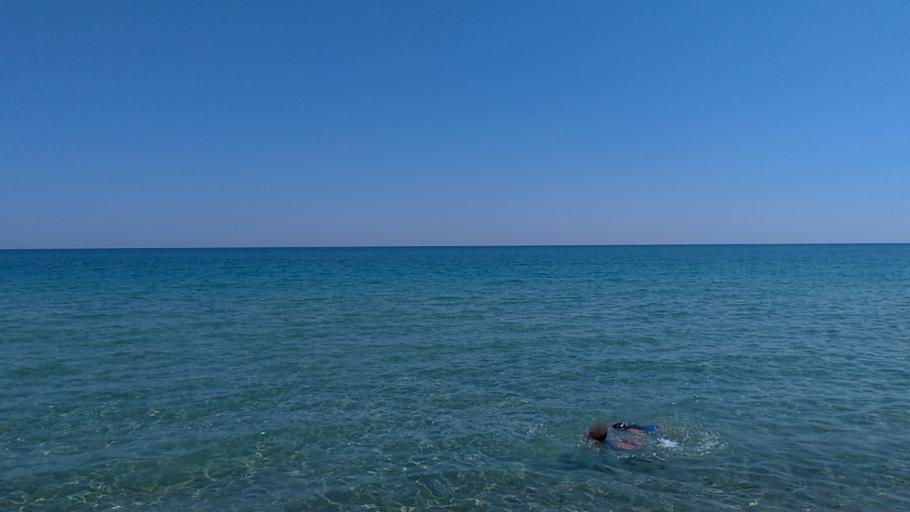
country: IT
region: Calabria
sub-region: Provincia di Crotone
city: Torre Melissa
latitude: 39.2819
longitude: 17.1090
